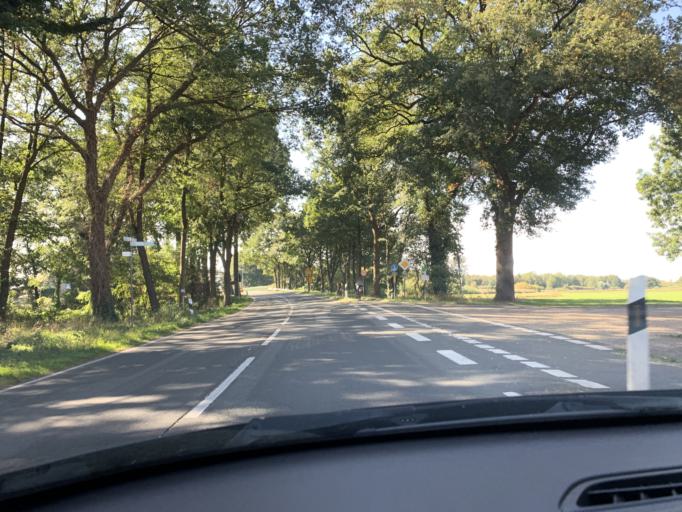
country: DE
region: Lower Saxony
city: Barssel
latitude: 53.1743
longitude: 7.7550
